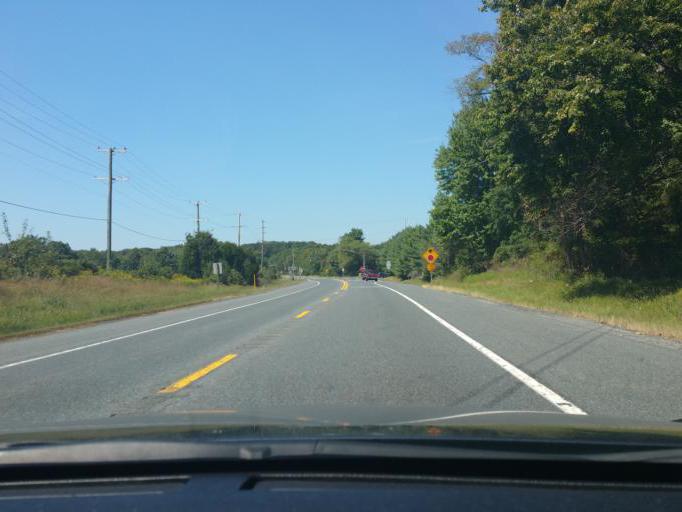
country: US
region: Maryland
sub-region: Harford County
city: Aberdeen
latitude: 39.5758
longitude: -76.1845
